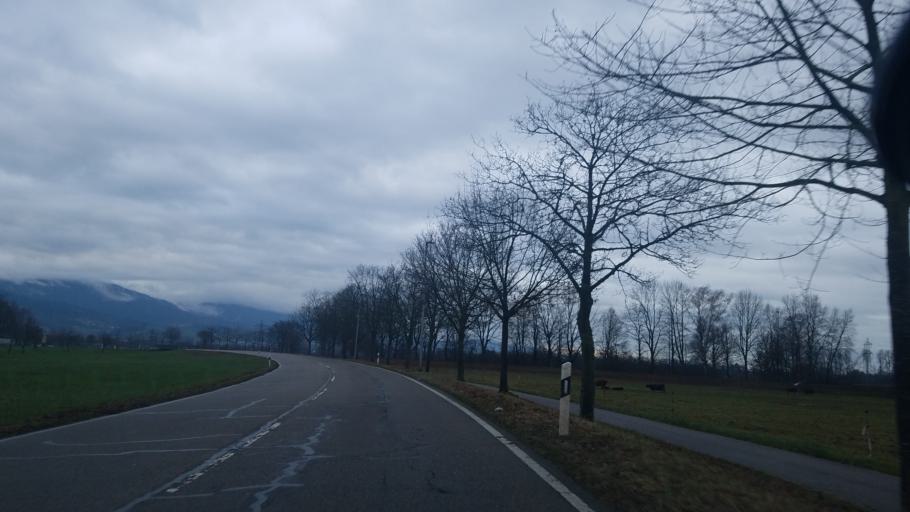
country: DE
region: Baden-Wuerttemberg
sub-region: Karlsruhe Region
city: Buhl
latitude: 48.7119
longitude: 8.1148
